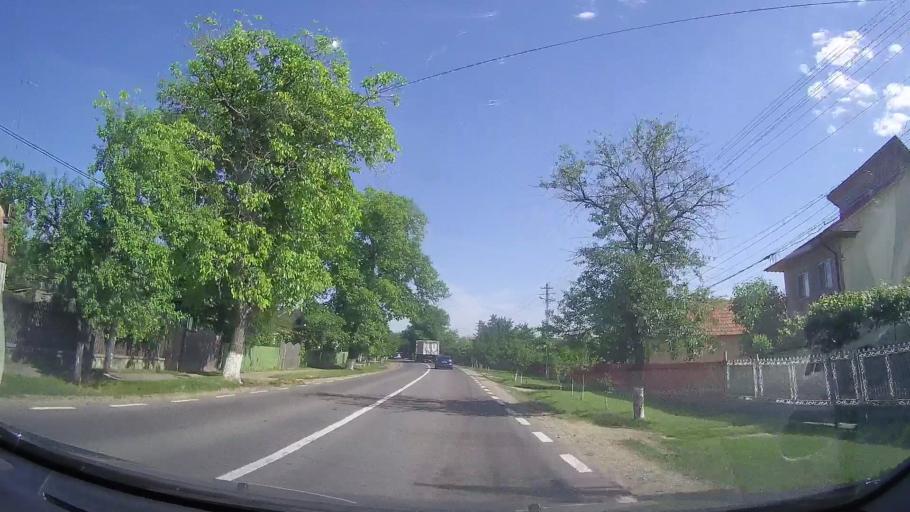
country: RO
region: Prahova
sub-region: Comuna Izvoarele
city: Homoraciu
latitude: 45.2579
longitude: 26.0185
